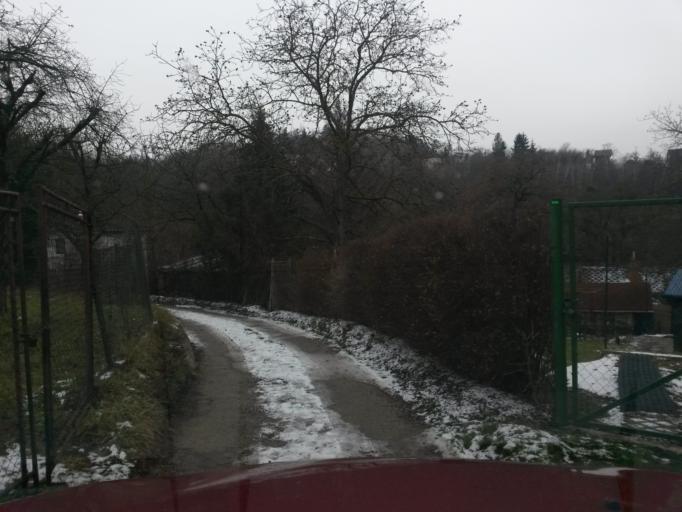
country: SK
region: Kosicky
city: Kosice
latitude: 48.7158
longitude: 21.2829
